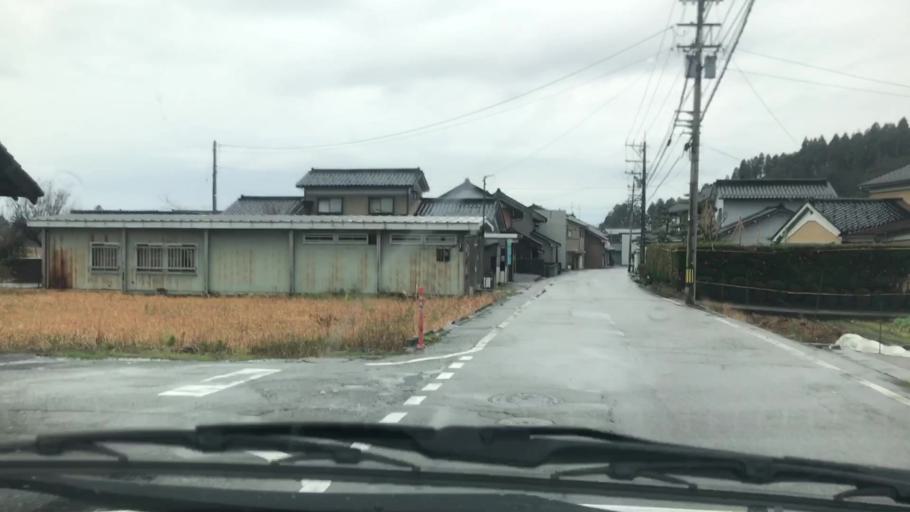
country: JP
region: Toyama
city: Kamiichi
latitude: 36.6038
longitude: 137.2940
